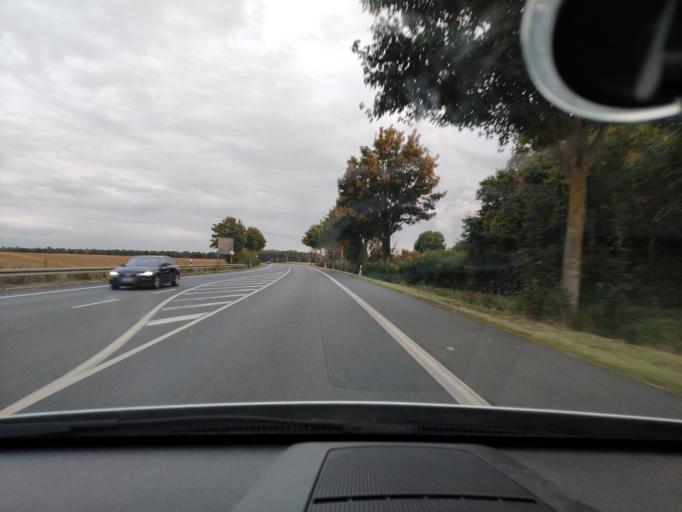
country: DE
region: North Rhine-Westphalia
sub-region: Regierungsbezirk Koln
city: Aldenhoven
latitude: 50.9054
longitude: 6.2629
